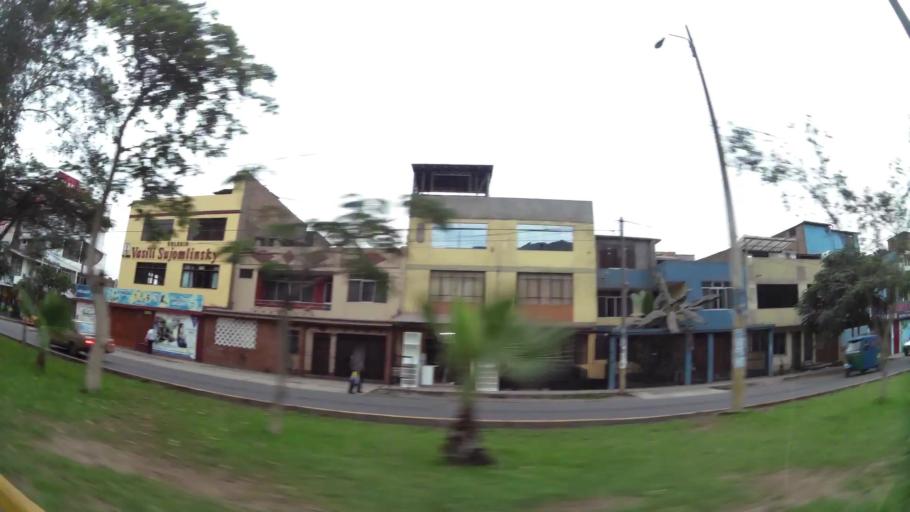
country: PE
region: Lima
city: Lima
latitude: -12.0188
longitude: -76.9841
